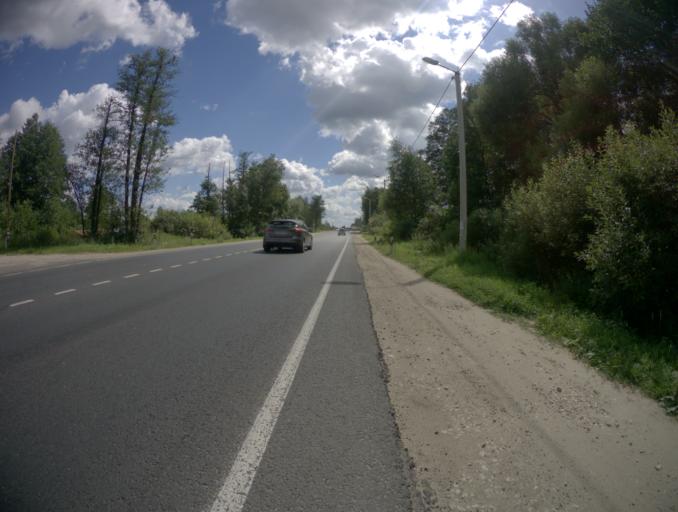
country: RU
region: Vladimir
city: Kommunar
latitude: 56.0488
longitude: 40.5332
